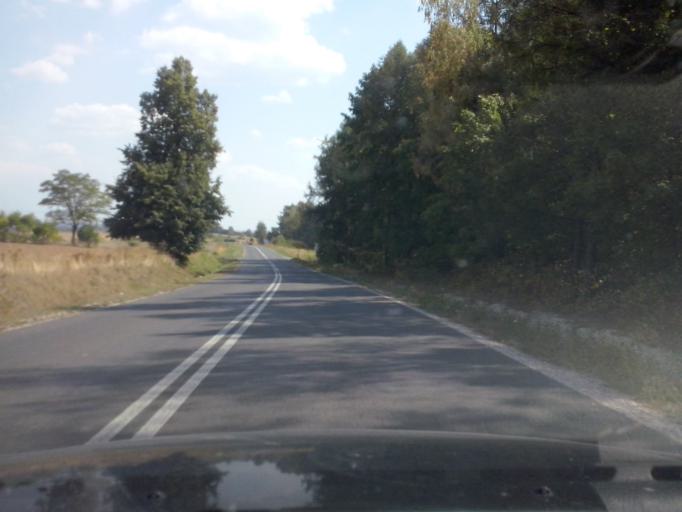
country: PL
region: Swietokrzyskie
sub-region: Powiat staszowski
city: Szydlow
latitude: 50.5829
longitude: 21.0626
